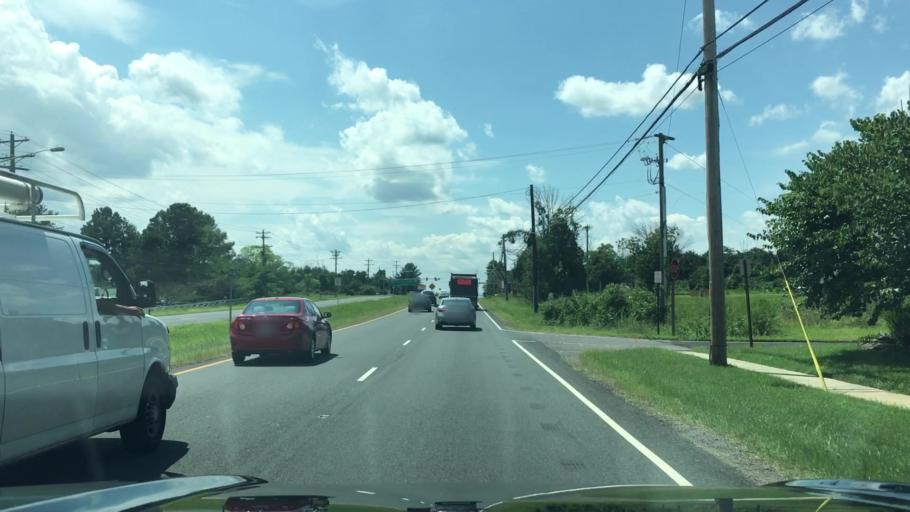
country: US
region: Virginia
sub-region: Prince William County
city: Sudley
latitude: 38.8288
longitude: -77.4829
